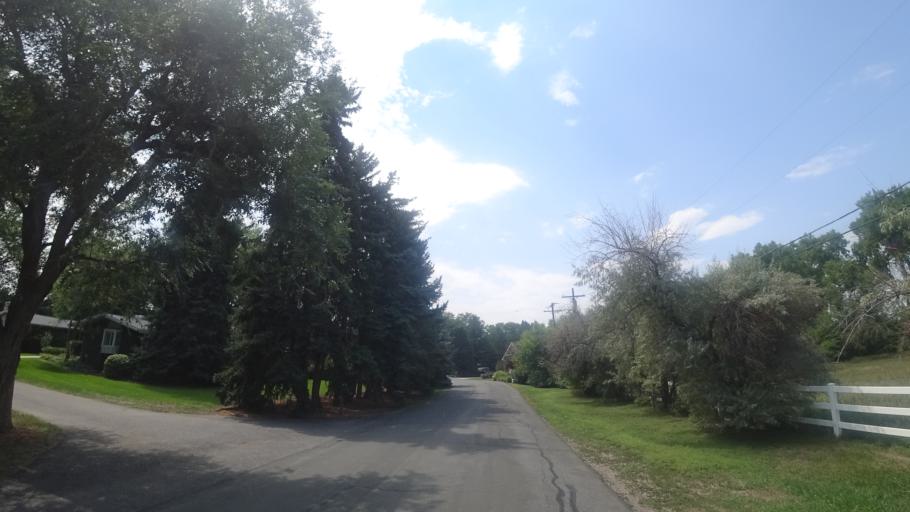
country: US
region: Colorado
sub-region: Arapahoe County
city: Greenwood Village
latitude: 39.6180
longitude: -104.9733
